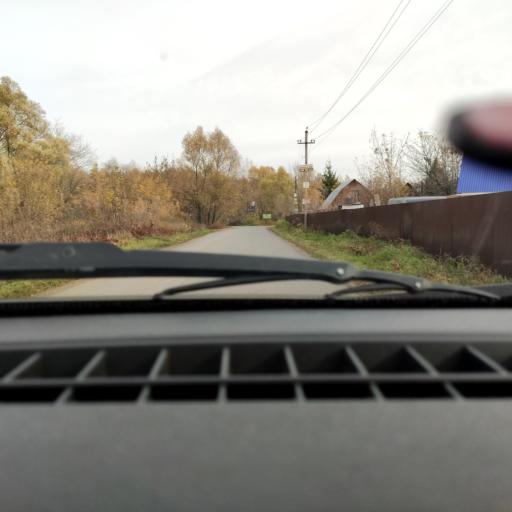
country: RU
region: Bashkortostan
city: Iglino
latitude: 54.8126
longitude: 56.1913
